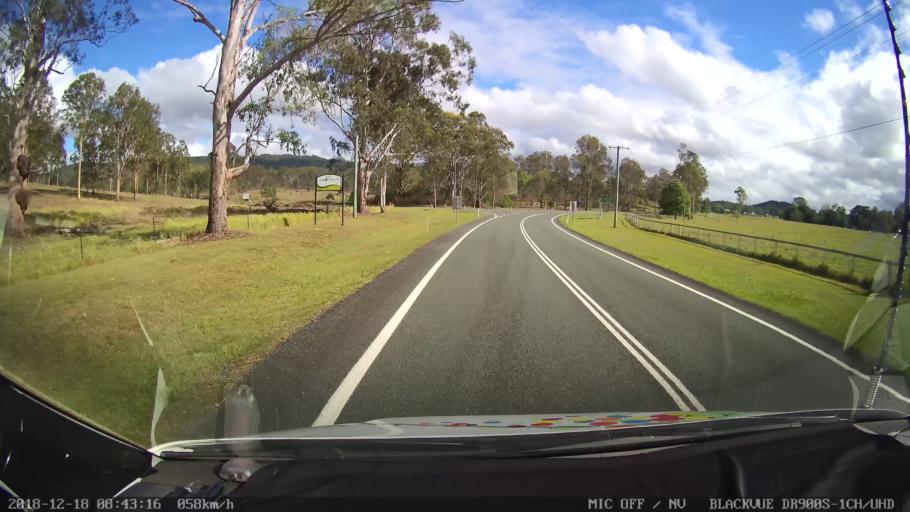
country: AU
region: Queensland
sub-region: Logan
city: Cedar Vale
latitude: -28.2197
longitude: 152.8583
